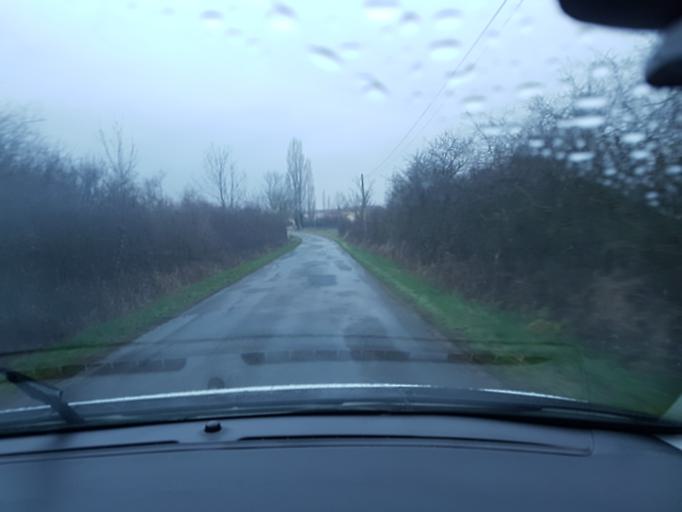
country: FR
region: Rhone-Alpes
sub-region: Departement du Rhone
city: Mornant
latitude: 45.6101
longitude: 4.6919
